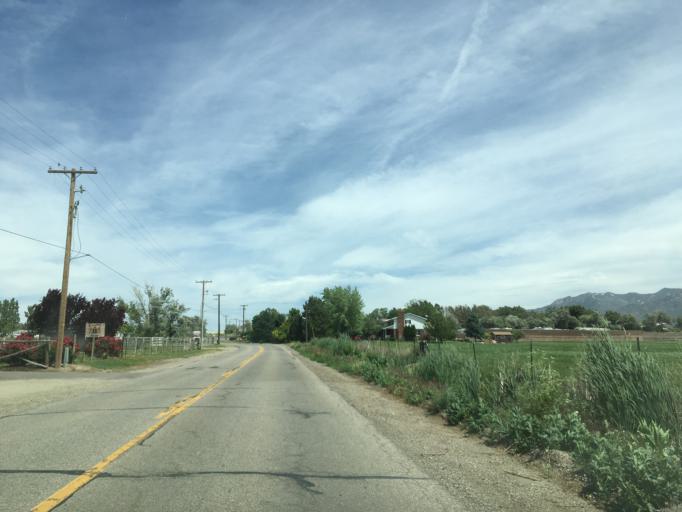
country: US
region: Utah
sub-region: Davis County
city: Hill Air Force Bace
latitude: 41.0947
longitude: -111.9596
